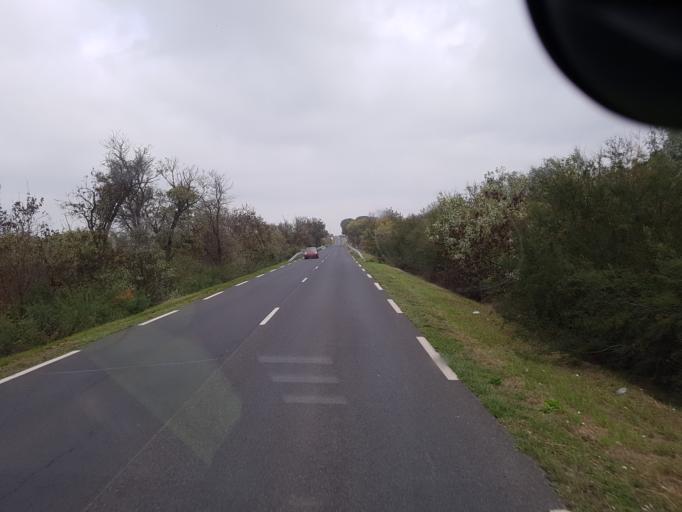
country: FR
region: Languedoc-Roussillon
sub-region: Departement de l'Herault
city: Marseillan
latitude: 43.3835
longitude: 3.5359
